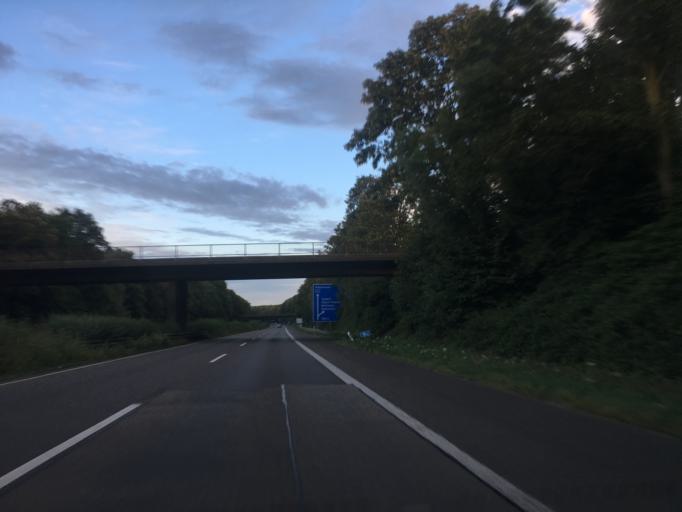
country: DE
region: North Rhine-Westphalia
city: Siersdorf
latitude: 50.8599
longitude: 6.2097
